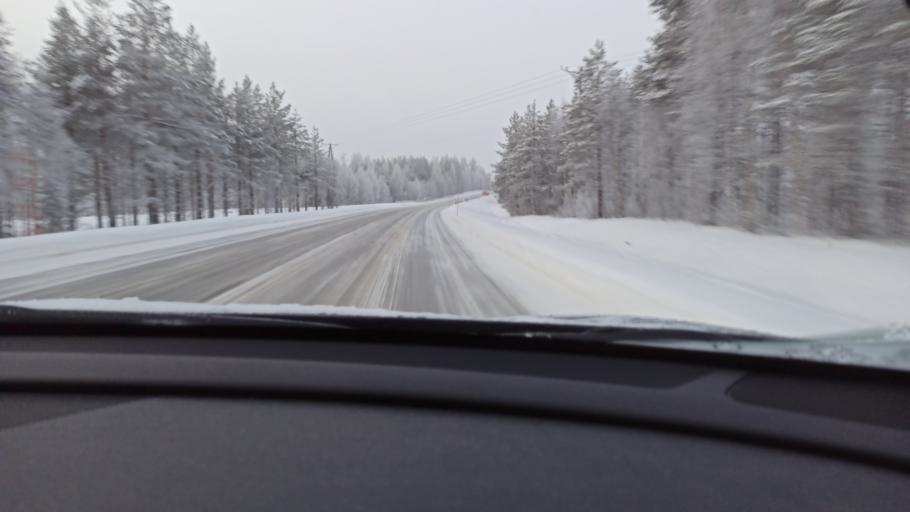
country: FI
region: Lapland
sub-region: Pohjois-Lappi
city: Sodankylae
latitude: 66.9301
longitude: 26.2534
